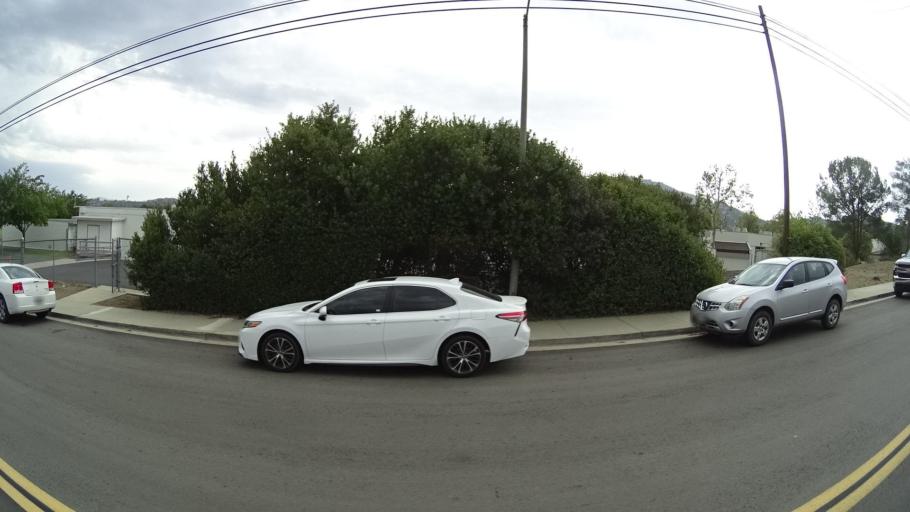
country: US
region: California
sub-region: San Diego County
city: San Pasqual
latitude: 33.0332
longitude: -116.9569
